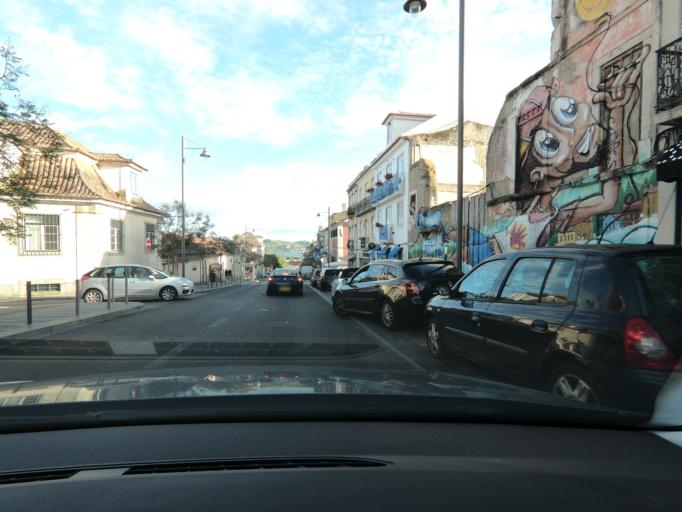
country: PT
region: Lisbon
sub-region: Oeiras
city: Alges
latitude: 38.7035
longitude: -9.1995
